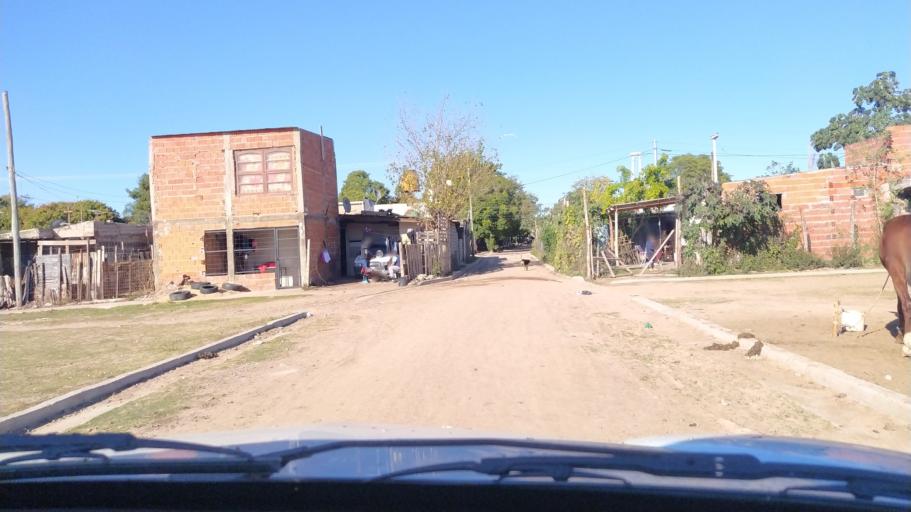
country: AR
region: Corrientes
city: Corrientes
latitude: -27.4988
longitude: -58.8091
